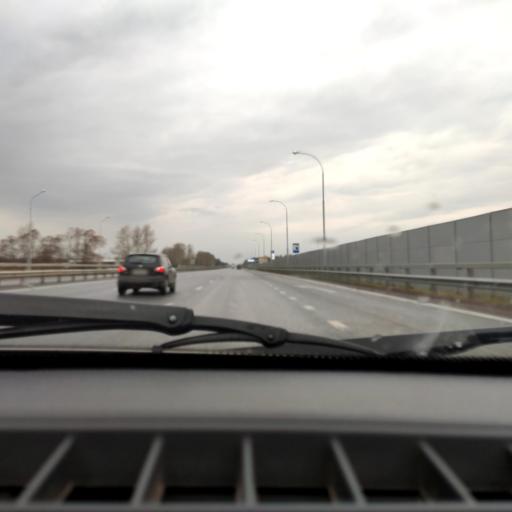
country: RU
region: Bashkortostan
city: Ufa
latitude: 54.6502
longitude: 56.0688
